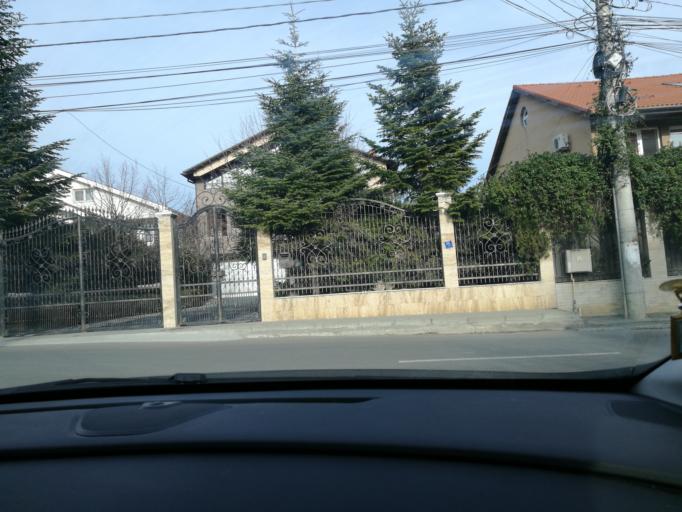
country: RO
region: Constanta
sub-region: Municipiul Constanta
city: Constanta
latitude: 44.1796
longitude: 28.6140
